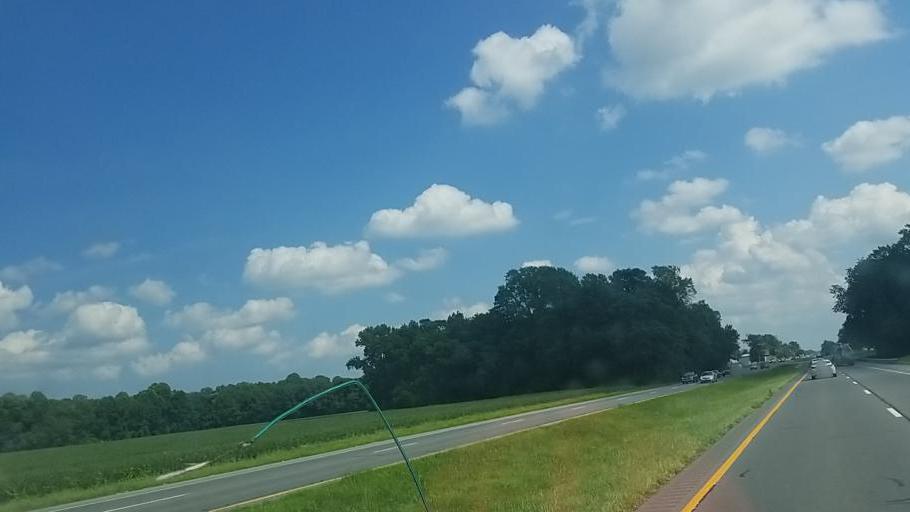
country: US
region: Delaware
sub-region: Sussex County
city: Georgetown
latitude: 38.6411
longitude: -75.3569
